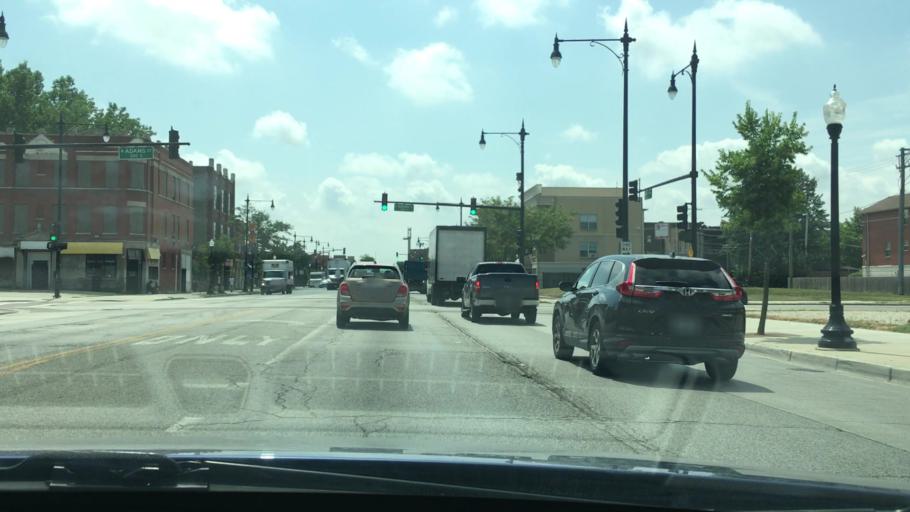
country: US
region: Illinois
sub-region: Cook County
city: Chicago
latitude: 41.8790
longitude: -87.6864
